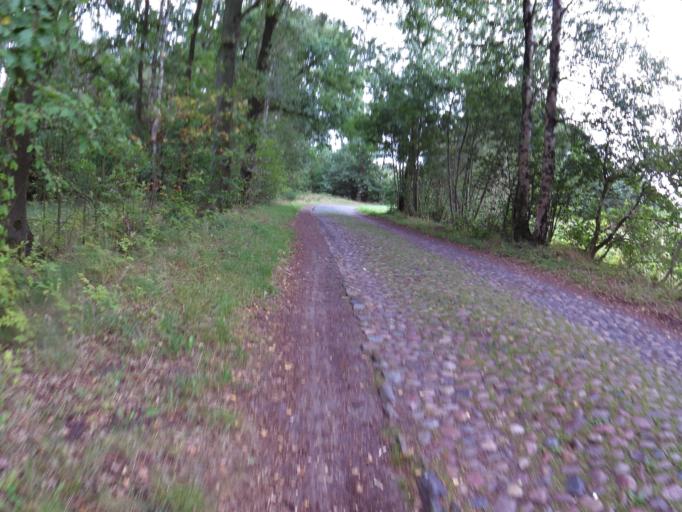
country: DE
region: Lower Saxony
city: Rotenburg
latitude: 53.1374
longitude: 9.4389
